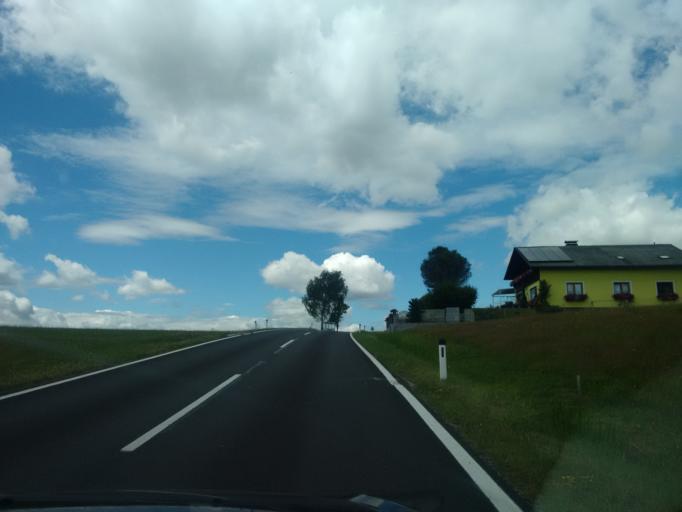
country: AT
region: Upper Austria
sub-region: Politischer Bezirk Urfahr-Umgebung
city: Gramastetten
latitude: 48.4082
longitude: 14.1735
